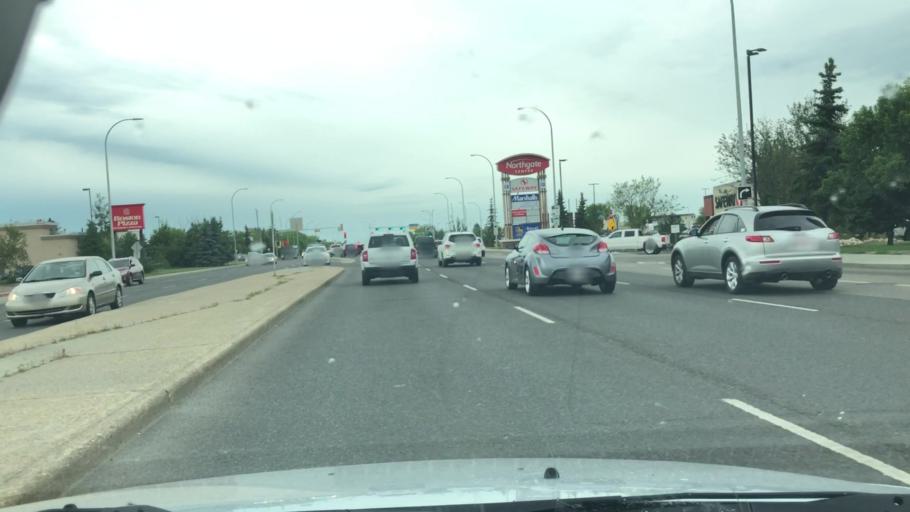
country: CA
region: Alberta
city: Edmonton
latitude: 53.5975
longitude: -113.4919
